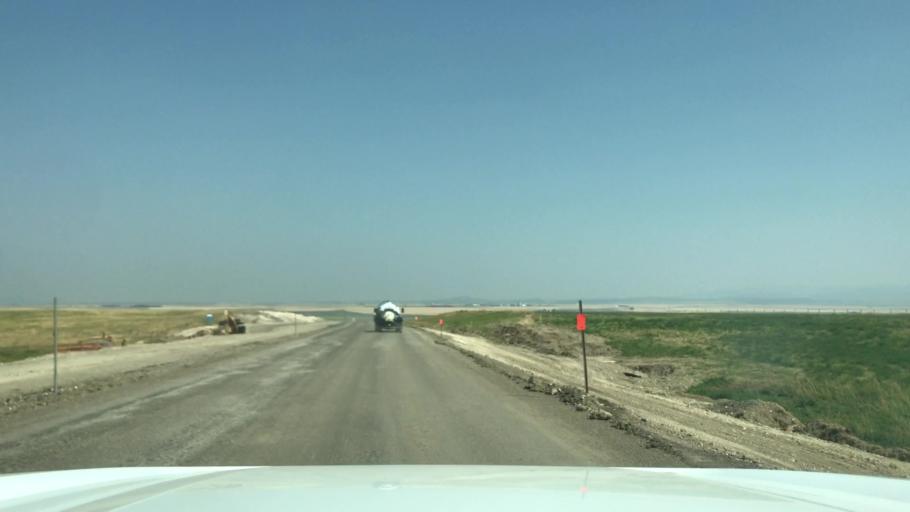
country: US
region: Montana
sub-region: Fergus County
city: Lewistown
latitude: 46.9986
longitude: -109.8144
